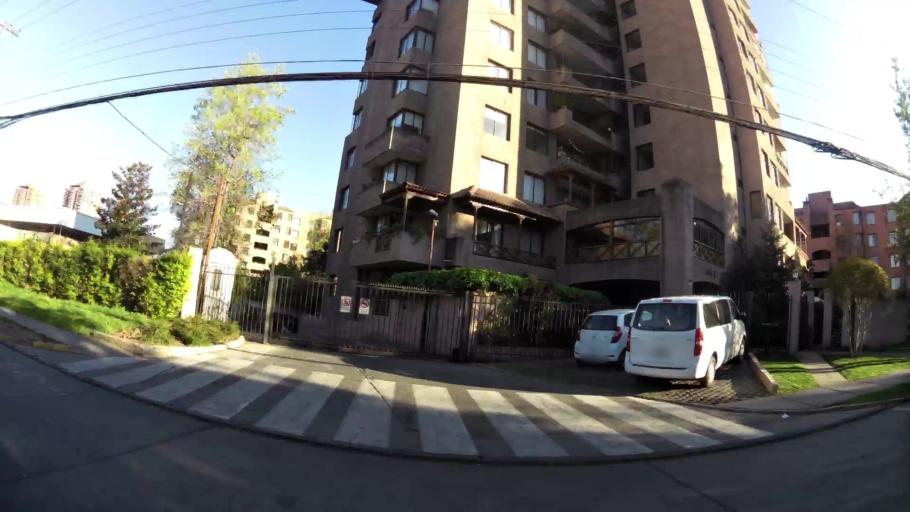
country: CL
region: Santiago Metropolitan
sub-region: Provincia de Santiago
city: Villa Presidente Frei, Nunoa, Santiago, Chile
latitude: -33.4003
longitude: -70.5648
